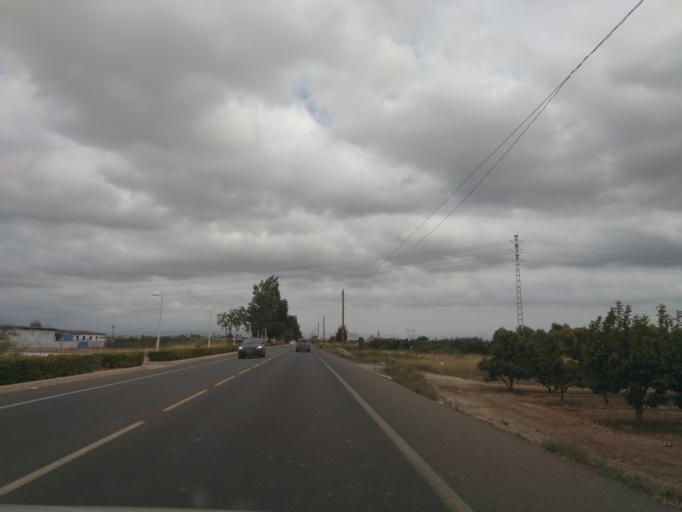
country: ES
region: Valencia
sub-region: Provincia de Valencia
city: Carlet
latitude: 39.2158
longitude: -0.5151
